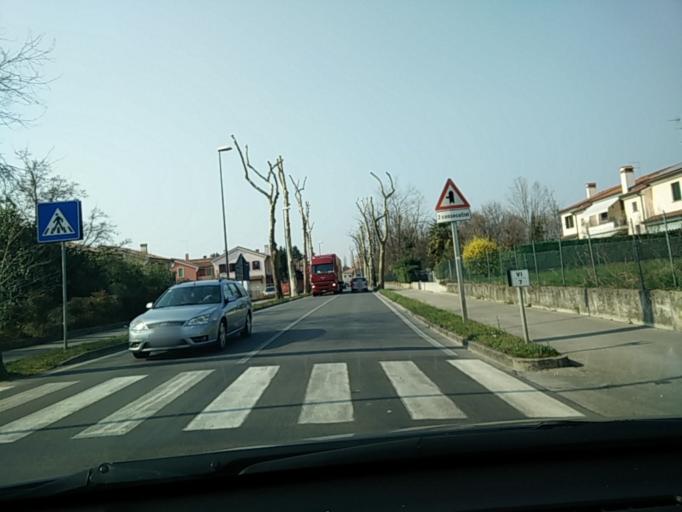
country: IT
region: Veneto
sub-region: Provincia di Treviso
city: Postioma
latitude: 45.7159
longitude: 12.1564
